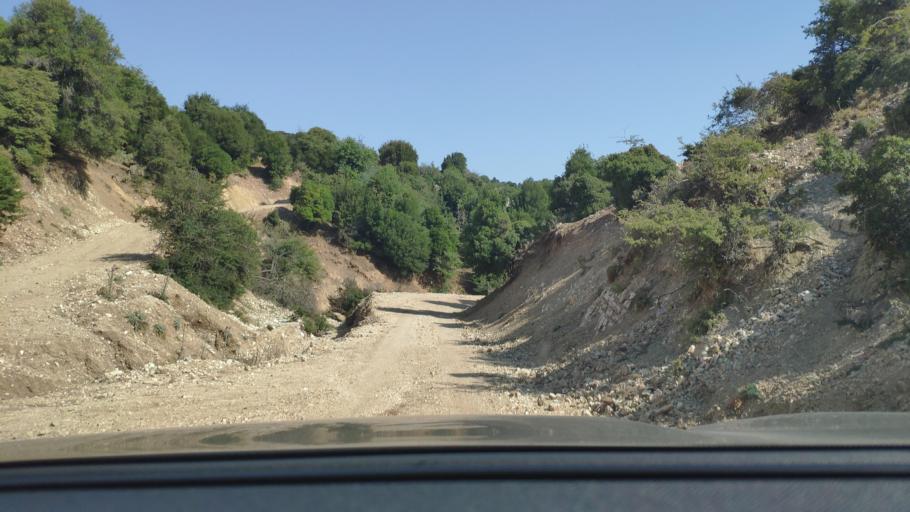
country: GR
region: West Greece
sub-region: Nomos Aitolias kai Akarnanias
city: Monastirakion
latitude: 38.8012
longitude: 20.9965
